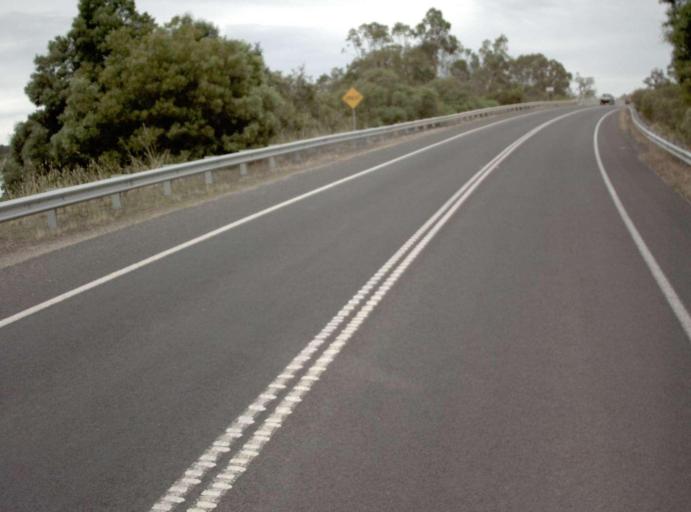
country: AU
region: Victoria
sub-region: Wellington
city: Sale
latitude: -38.1411
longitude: 147.0807
